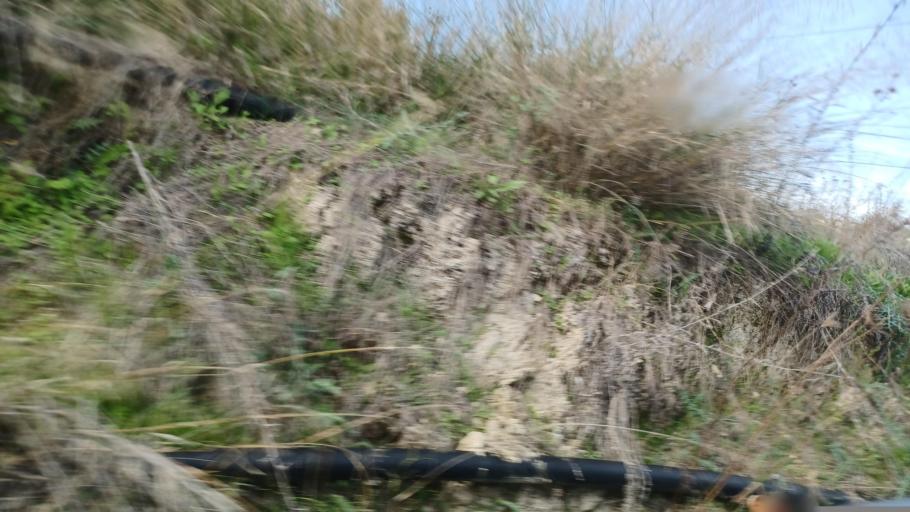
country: CY
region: Pafos
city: Mesogi
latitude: 34.8560
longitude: 32.5224
